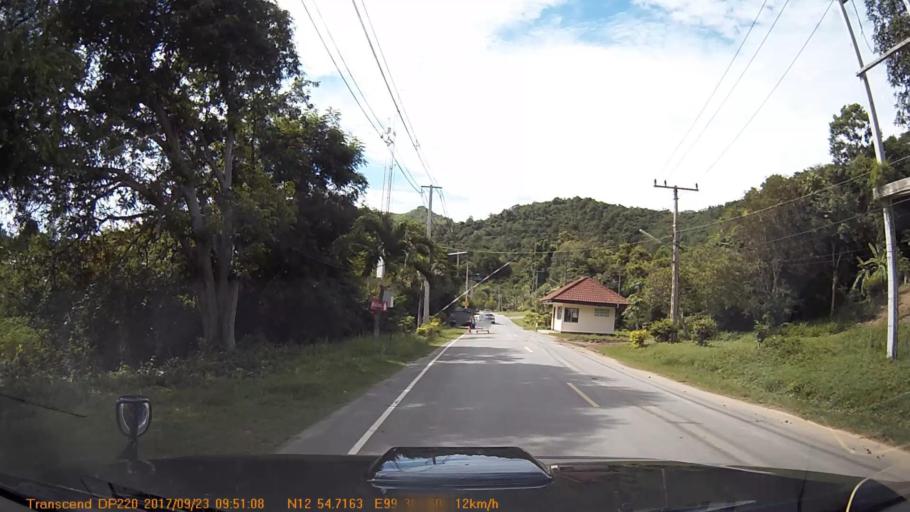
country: TH
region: Phetchaburi
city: Kaeng Krachan
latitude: 12.9129
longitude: 99.6406
